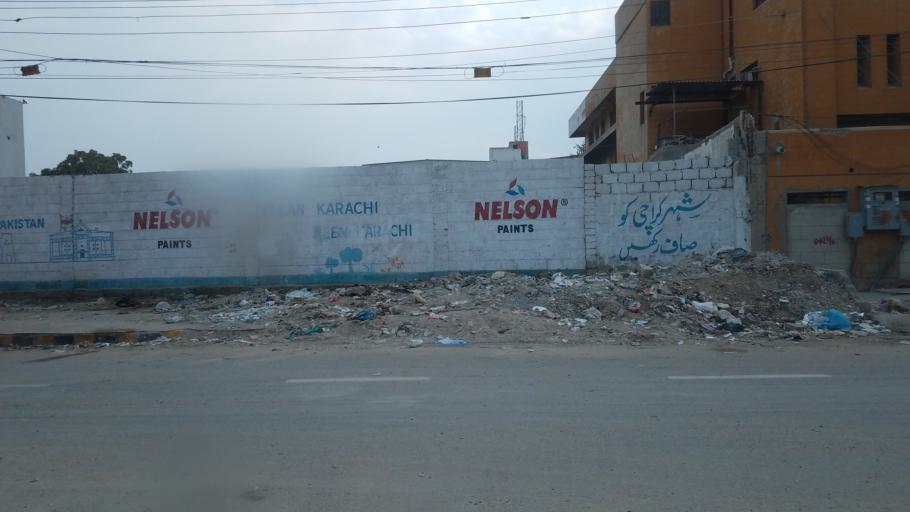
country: PK
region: Sindh
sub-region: Karachi District
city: Karachi
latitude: 24.9400
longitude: 67.0851
